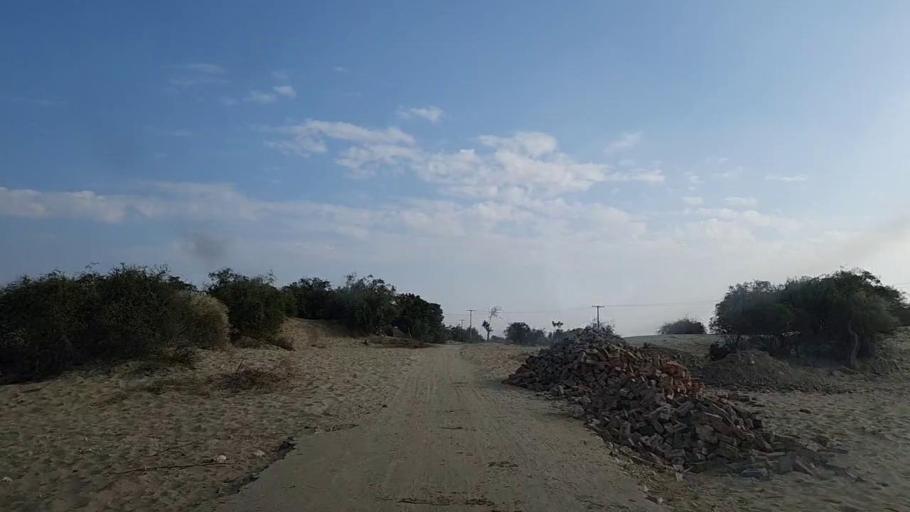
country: PK
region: Sindh
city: Sanghar
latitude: 26.2031
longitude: 69.0264
